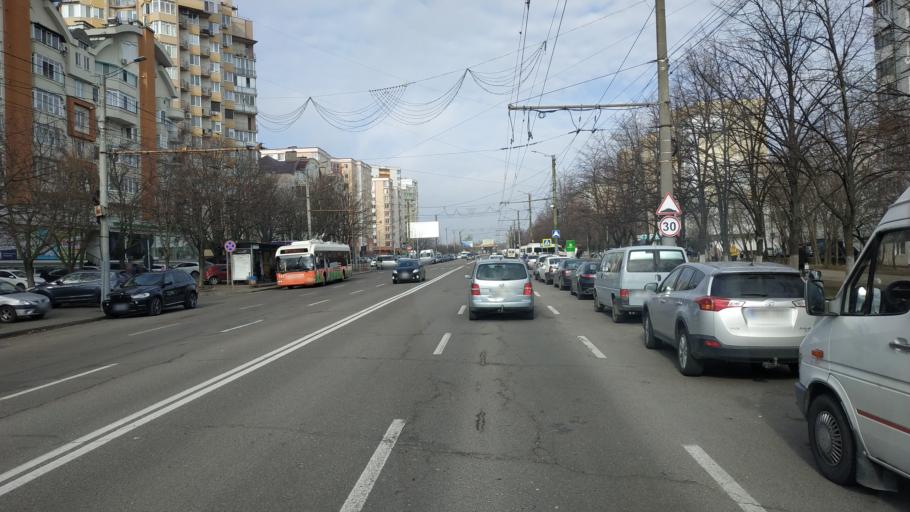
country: MD
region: Chisinau
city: Vatra
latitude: 47.0409
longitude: 28.7648
